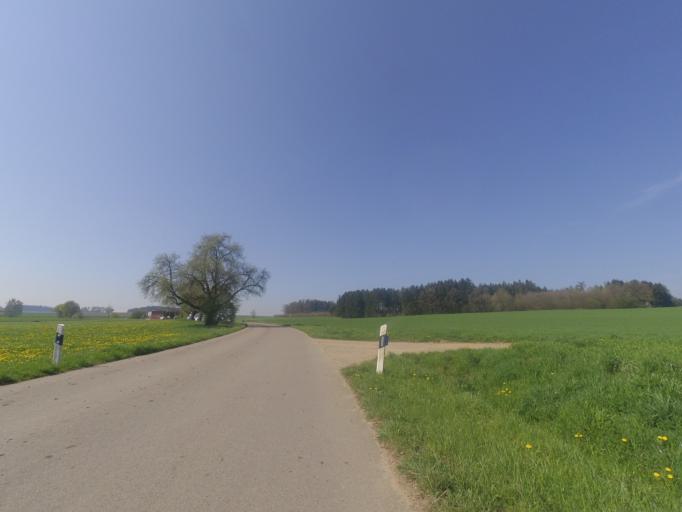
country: DE
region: Bavaria
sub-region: Swabia
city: Pfaffenhofen an der Roth
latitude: 48.3957
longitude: 10.1752
